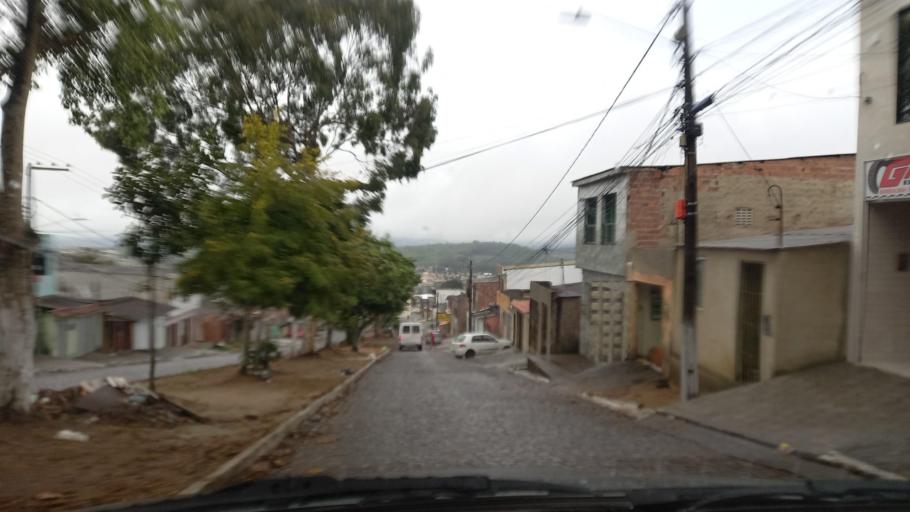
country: BR
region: Pernambuco
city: Garanhuns
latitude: -8.8826
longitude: -36.4998
